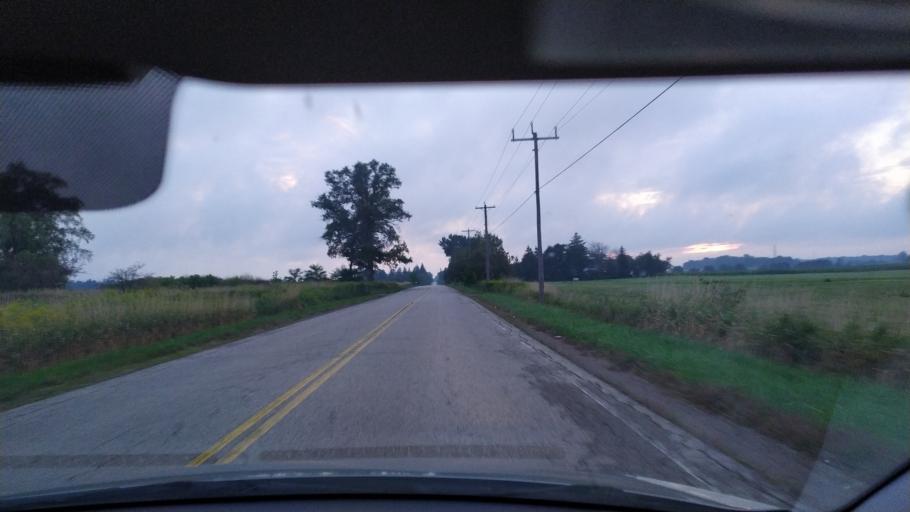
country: CA
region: Ontario
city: Kitchener
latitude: 43.3539
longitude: -80.6742
